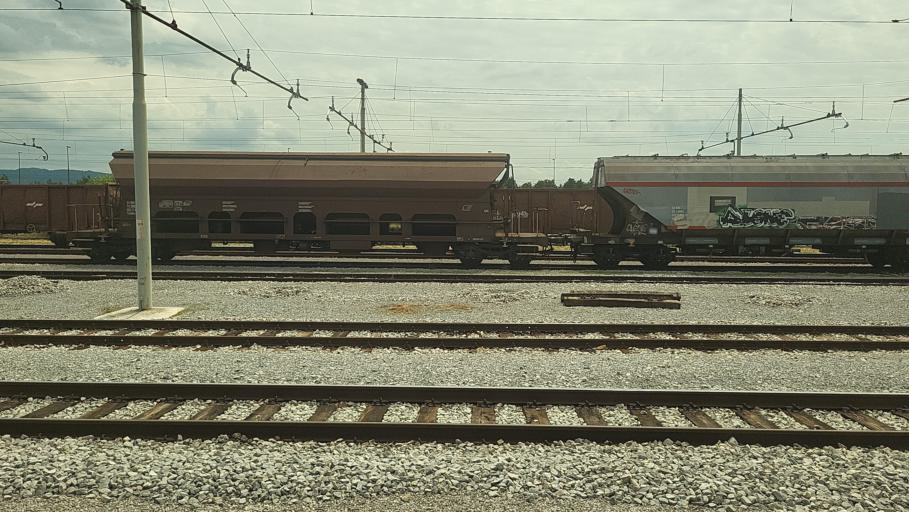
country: SI
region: Sezana
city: Sezana
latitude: 45.7040
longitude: 13.8611
